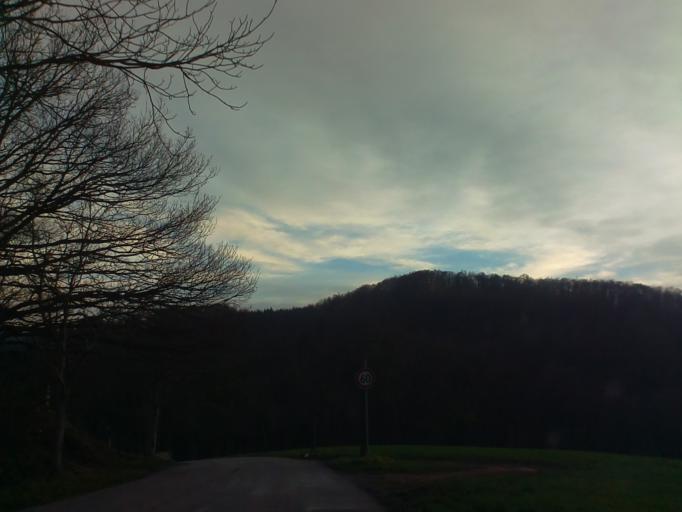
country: DE
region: Hesse
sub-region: Regierungsbezirk Darmstadt
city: Morlenbach
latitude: 49.5829
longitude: 8.7485
